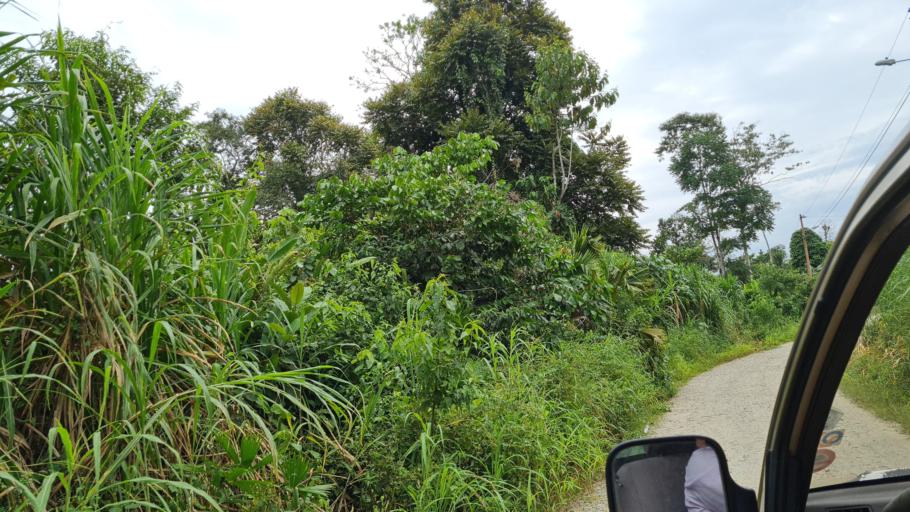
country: EC
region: Napo
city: Tena
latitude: -1.0002
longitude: -77.7606
